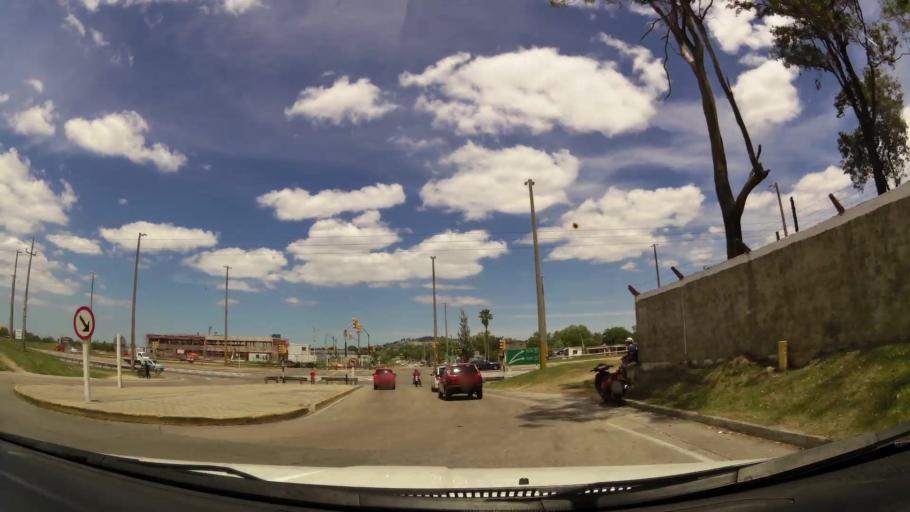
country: UY
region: Montevideo
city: Montevideo
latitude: -34.8637
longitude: -56.2524
